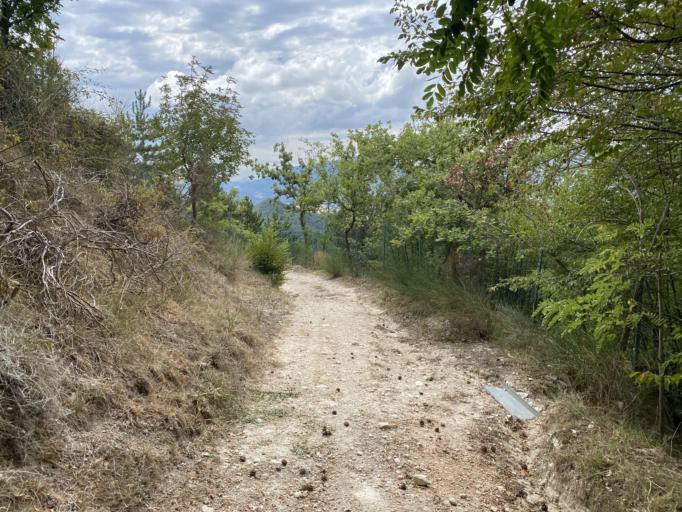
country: IT
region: The Marches
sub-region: Provincia di Pesaro e Urbino
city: Canavaccio
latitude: 43.7114
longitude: 12.7110
